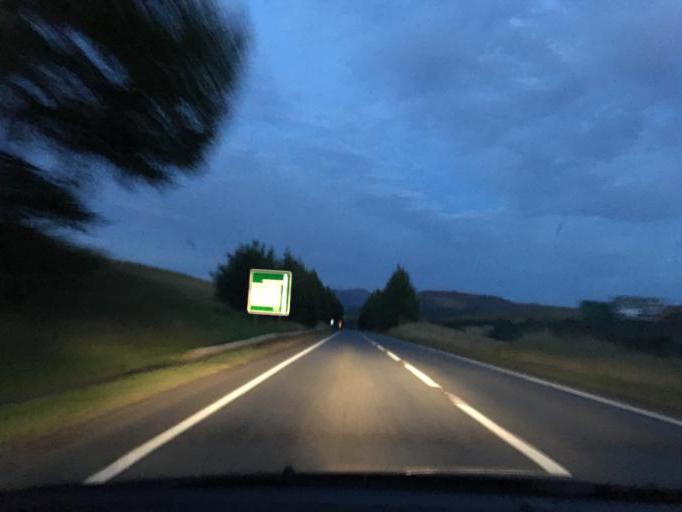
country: GB
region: Scotland
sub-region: Perth and Kinross
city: Aberfeldy
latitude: 56.7694
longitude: -3.9556
